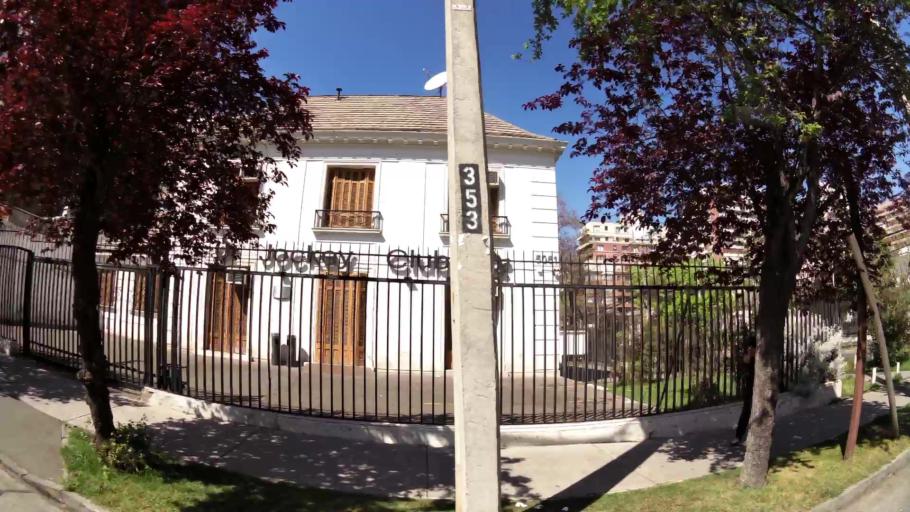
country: CL
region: Santiago Metropolitan
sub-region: Provincia de Santiago
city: Villa Presidente Frei, Nunoa, Santiago, Chile
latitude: -33.4115
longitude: -70.5757
